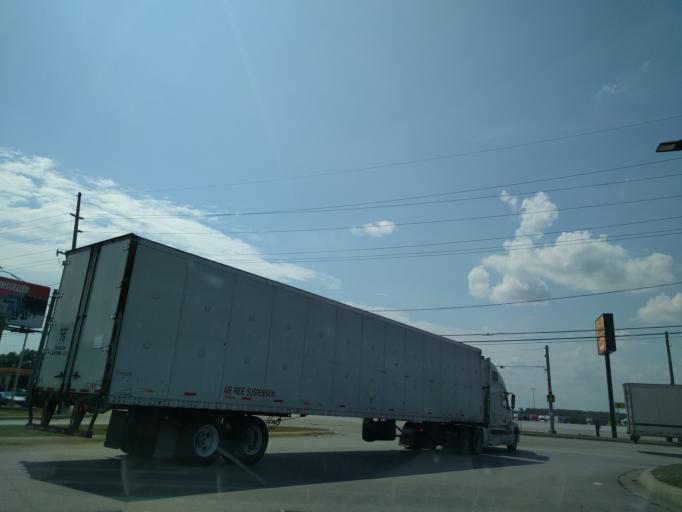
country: US
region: Indiana
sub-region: Lake County
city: Gary
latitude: 41.5629
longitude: -87.3555
